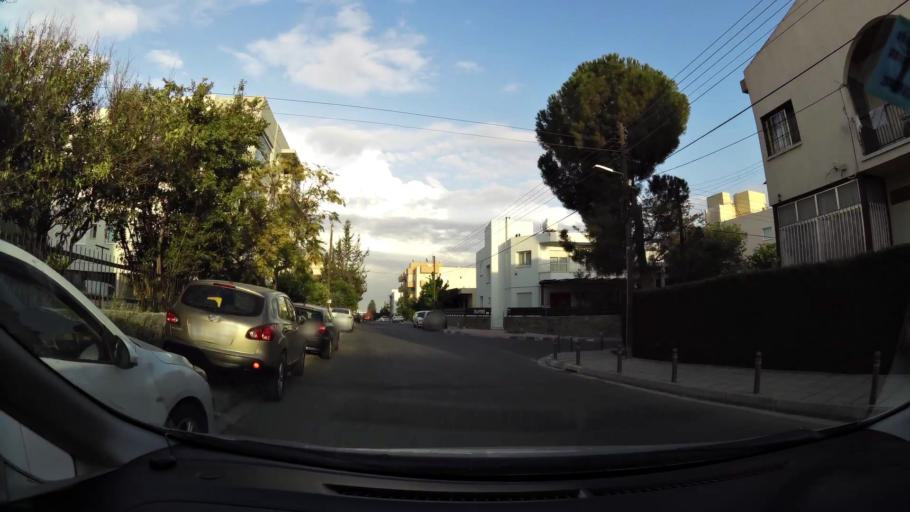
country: CY
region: Lefkosia
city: Nicosia
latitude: 35.1593
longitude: 33.3938
